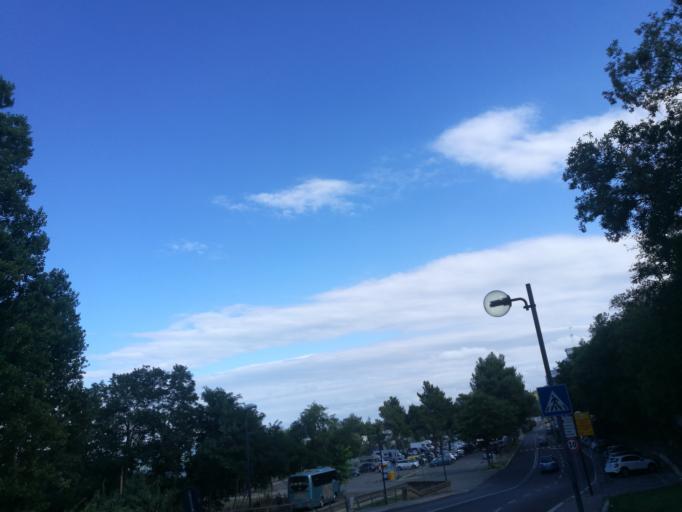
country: IT
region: Molise
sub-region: Provincia di Campobasso
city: Termoli
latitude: 41.9959
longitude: 14.9975
